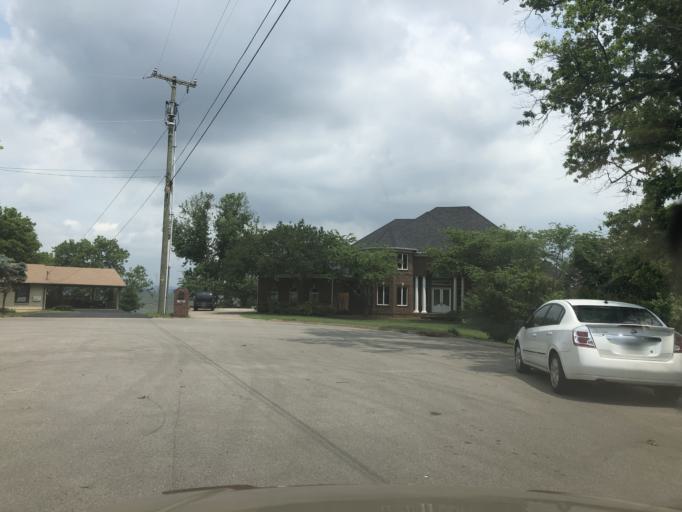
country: US
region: Tennessee
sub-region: Davidson County
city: Lakewood
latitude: 36.2431
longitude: -86.6226
